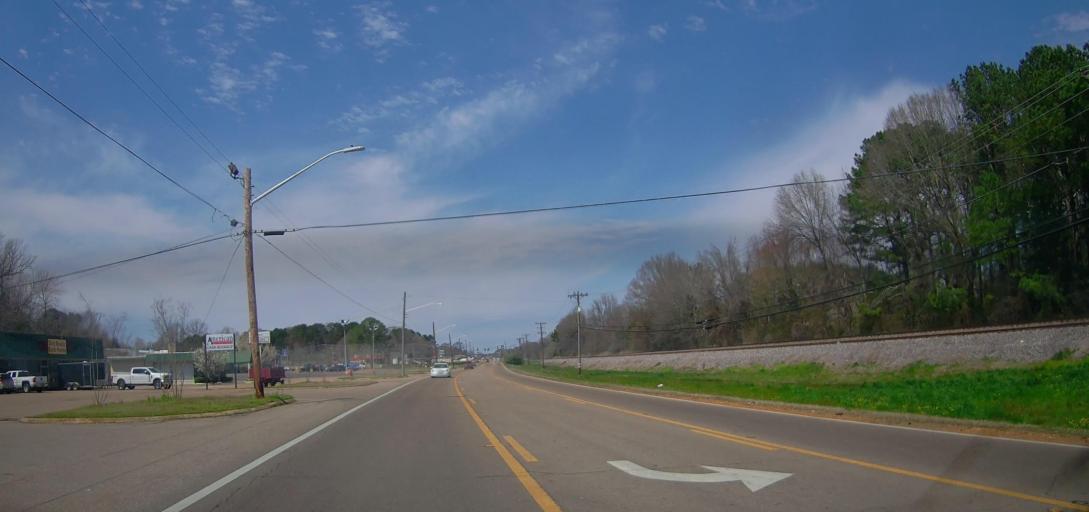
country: US
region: Mississippi
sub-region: Union County
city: New Albany
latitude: 34.4981
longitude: -89.0228
